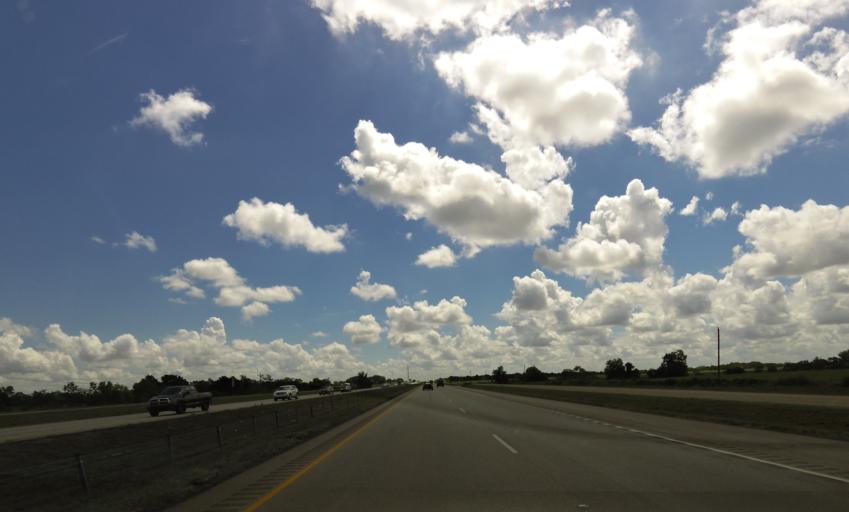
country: US
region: Texas
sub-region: Colorado County
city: Eagle Lake
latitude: 29.7298
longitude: -96.3879
